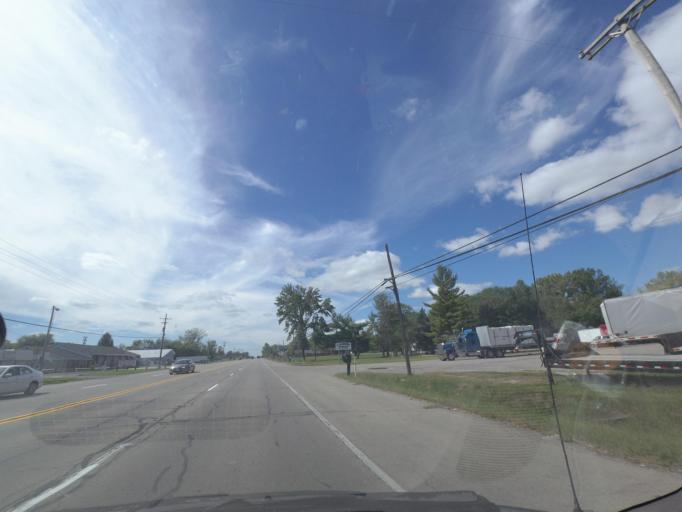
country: US
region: Indiana
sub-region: Hancock County
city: New Palestine
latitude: 39.7809
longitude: -85.8631
